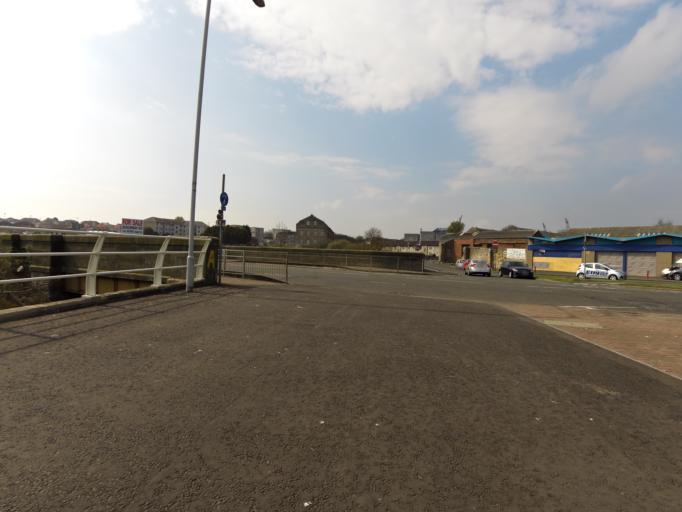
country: GB
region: Scotland
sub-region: Fife
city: Kirkcaldy
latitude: 56.0992
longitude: -3.1613
